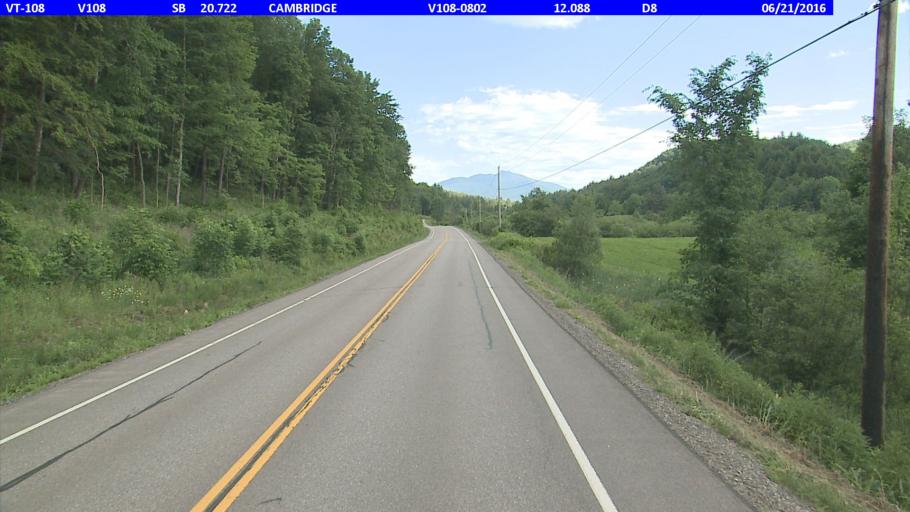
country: US
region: Vermont
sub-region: Lamoille County
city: Johnson
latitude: 44.6894
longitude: -72.8267
